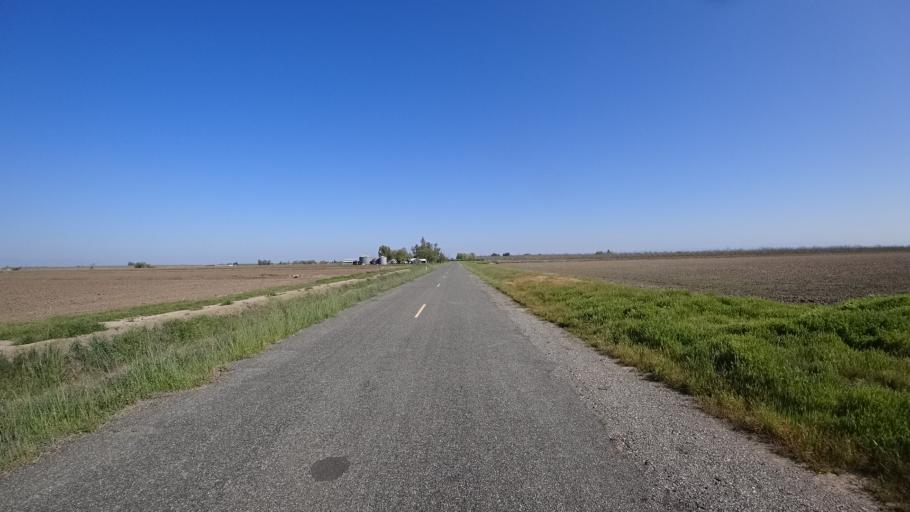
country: US
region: California
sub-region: Glenn County
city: Hamilton City
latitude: 39.6104
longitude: -122.0275
